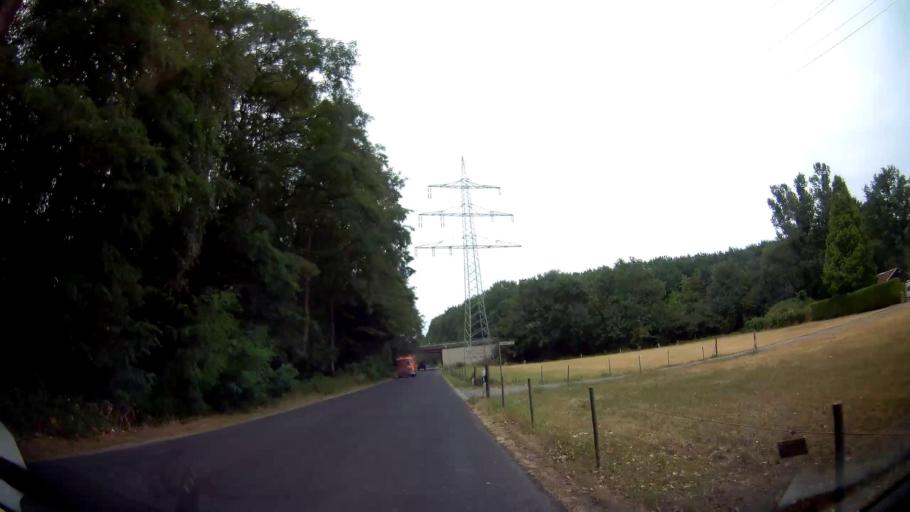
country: DE
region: North Rhine-Westphalia
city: Marl
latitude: 51.6704
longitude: 7.0726
